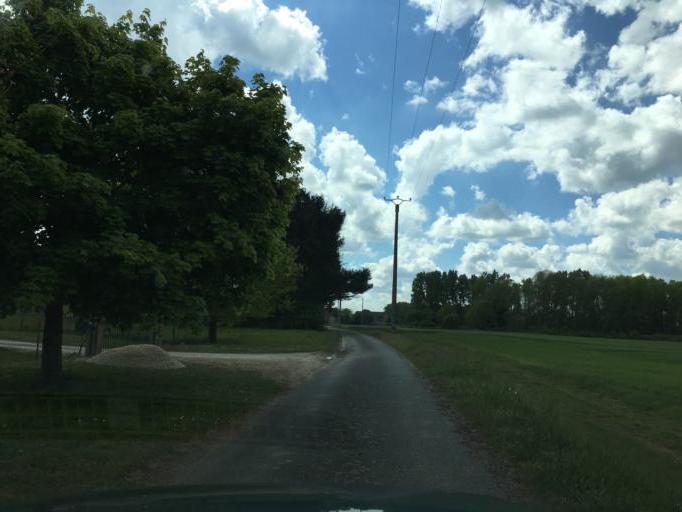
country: FR
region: Centre
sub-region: Departement du Loiret
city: Lailly-en-Val
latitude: 47.7810
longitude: 1.6619
